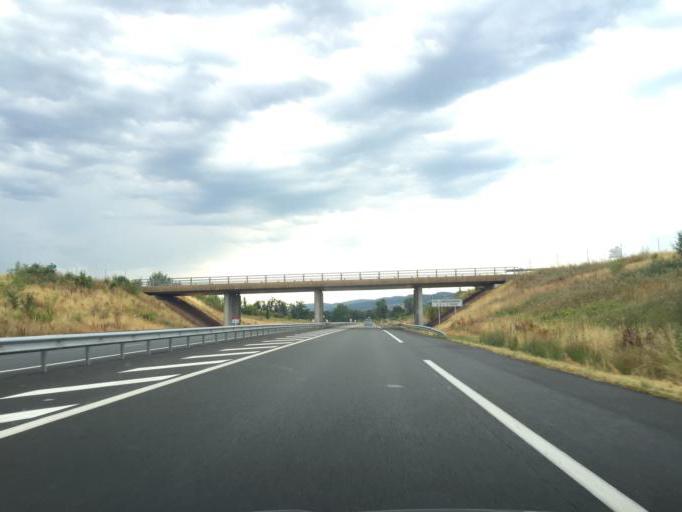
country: FR
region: Rhone-Alpes
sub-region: Departement de la Loire
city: Ambierle
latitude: 46.1415
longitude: 3.8996
